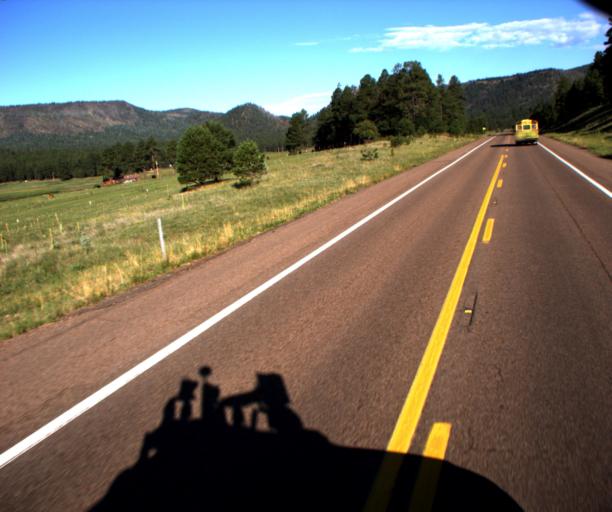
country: US
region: Arizona
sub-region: Apache County
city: Eagar
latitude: 33.8562
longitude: -109.1558
